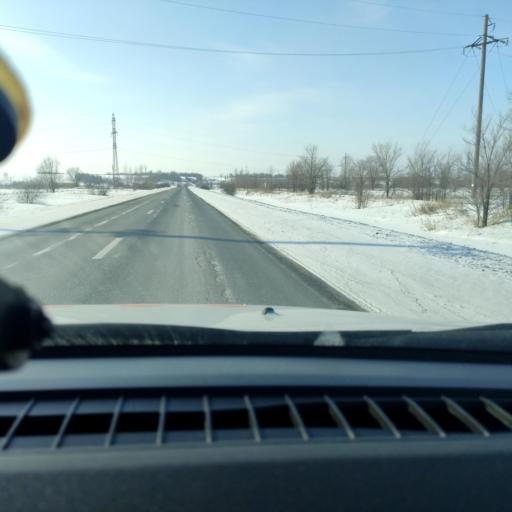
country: RU
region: Samara
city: Smyshlyayevka
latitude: 53.1555
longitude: 50.4212
